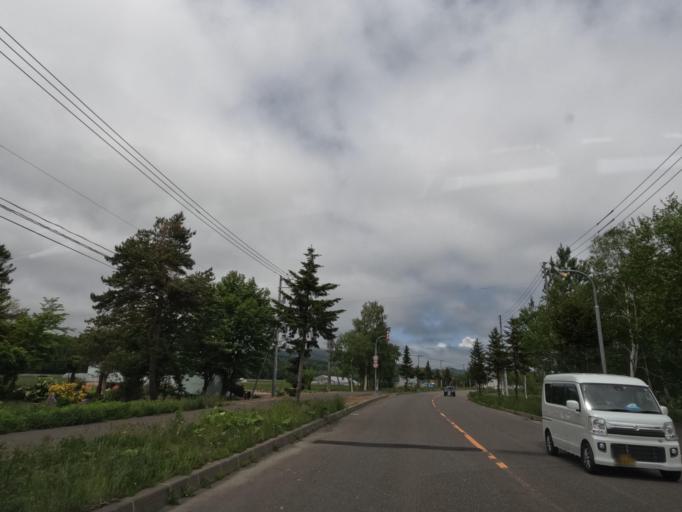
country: JP
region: Hokkaido
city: Tobetsu
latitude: 43.2581
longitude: 141.5236
